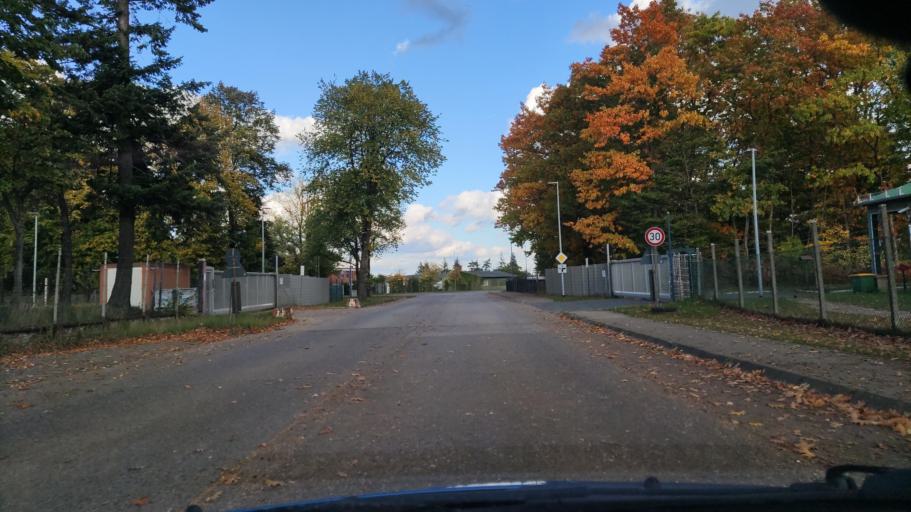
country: DE
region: Lower Saxony
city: Munster
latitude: 52.9845
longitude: 10.0707
